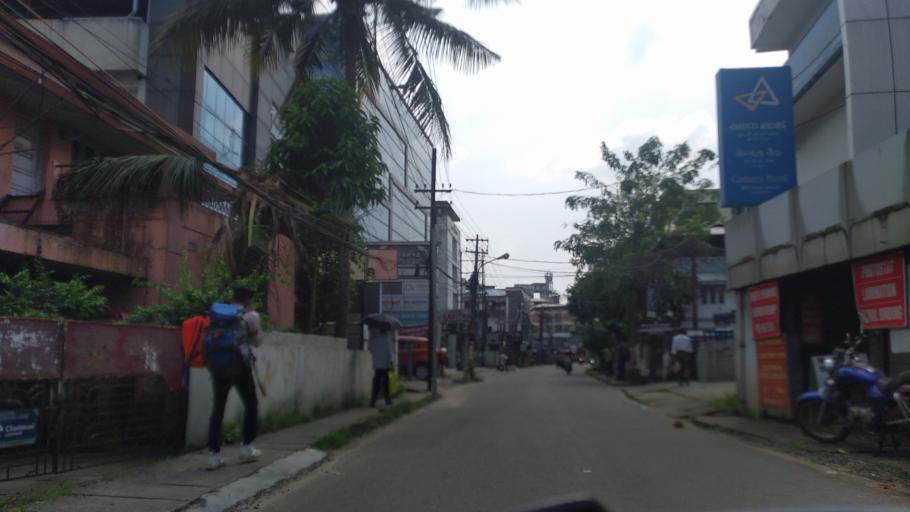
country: IN
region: Kerala
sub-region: Ernakulam
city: Cochin
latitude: 9.9739
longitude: 76.2859
